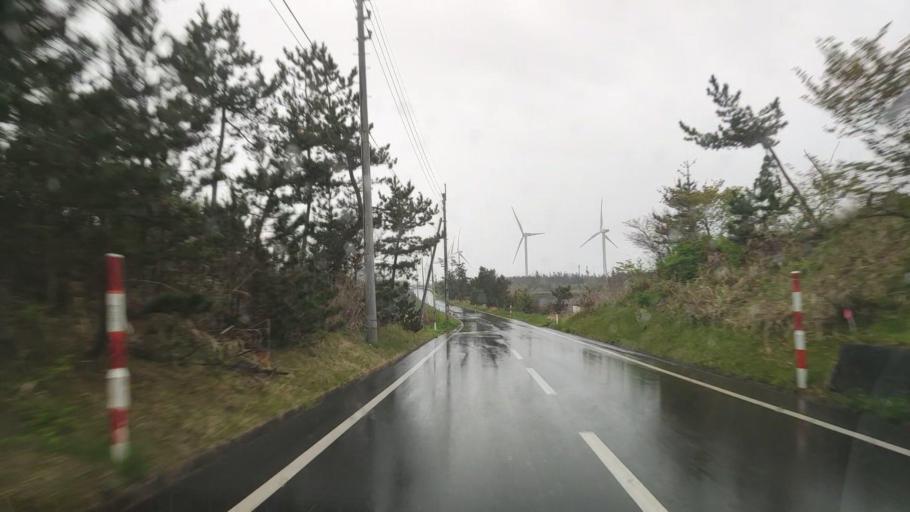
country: JP
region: Akita
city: Noshiromachi
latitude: 40.0787
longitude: 139.9535
